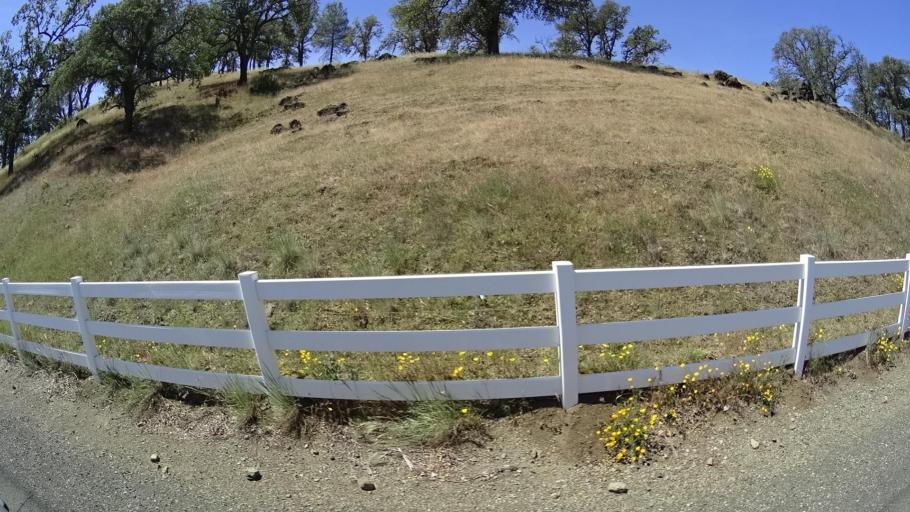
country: US
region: California
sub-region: Lake County
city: Hidden Valley Lake
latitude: 38.7269
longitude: -122.5167
